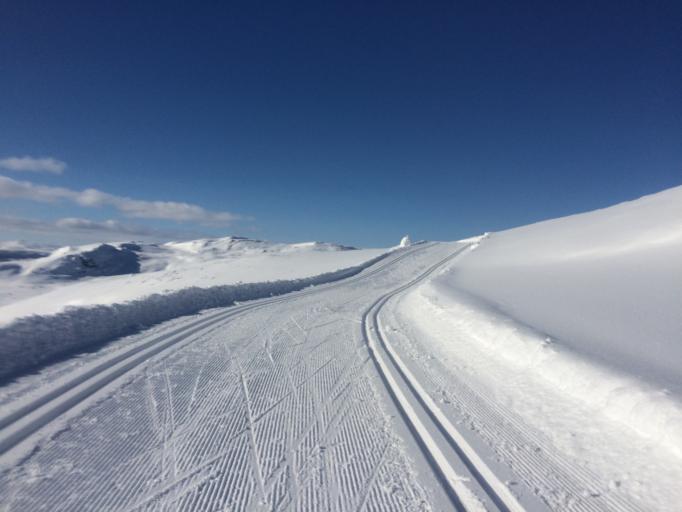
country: NO
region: Oppland
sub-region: Ringebu
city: Ringebu
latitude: 61.3713
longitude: 10.0718
